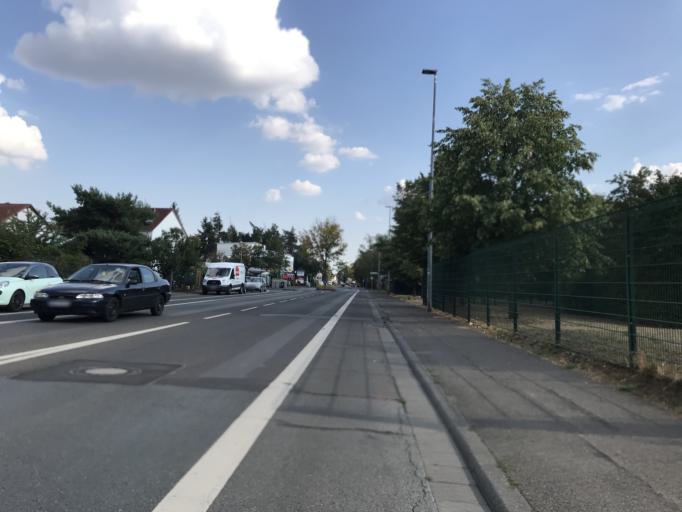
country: DE
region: Rheinland-Pfalz
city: Mainz
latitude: 50.0104
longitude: 8.2991
